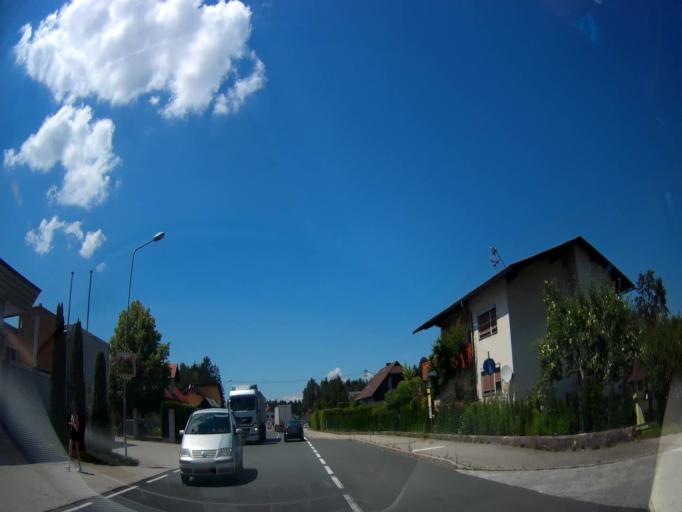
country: AT
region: Carinthia
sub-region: Politischer Bezirk Volkermarkt
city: Globasnitz
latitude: 46.6059
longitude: 14.7113
